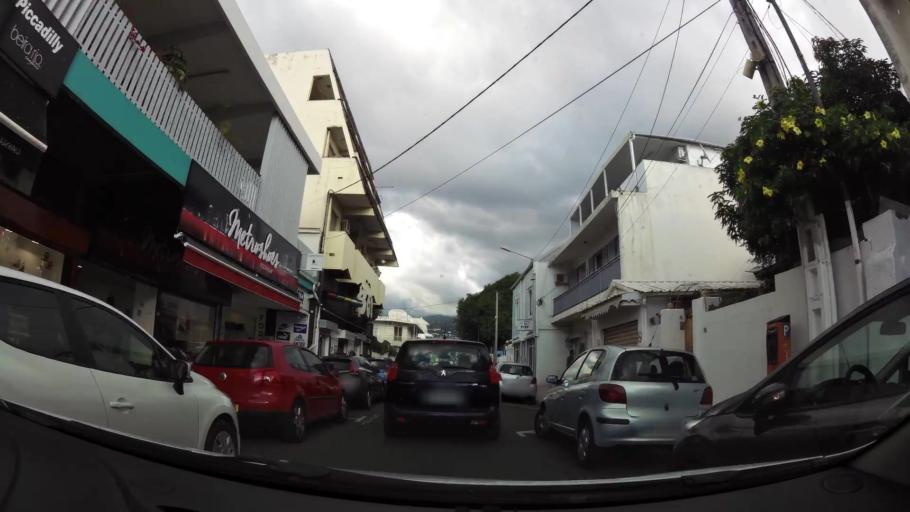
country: RE
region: Reunion
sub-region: Reunion
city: Saint-Denis
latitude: -20.8793
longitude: 55.4544
